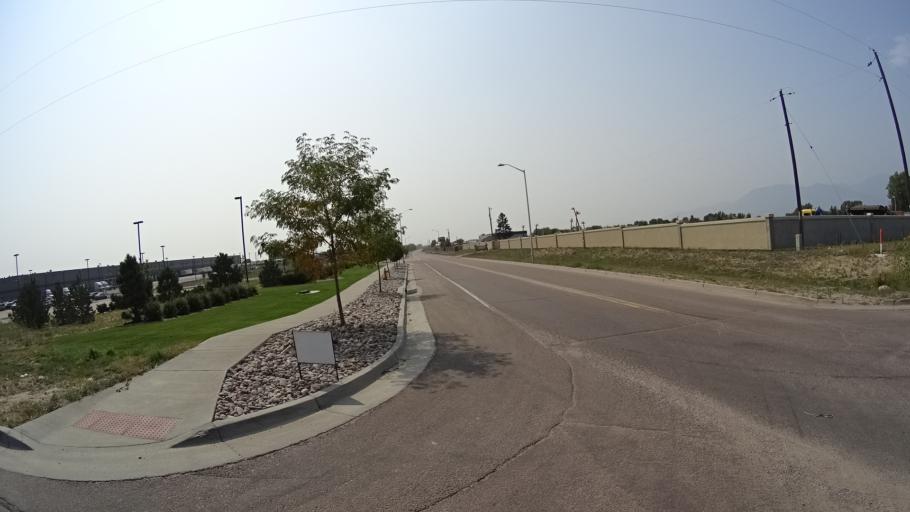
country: US
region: Colorado
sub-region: El Paso County
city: Cimarron Hills
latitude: 38.8357
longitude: -104.7247
